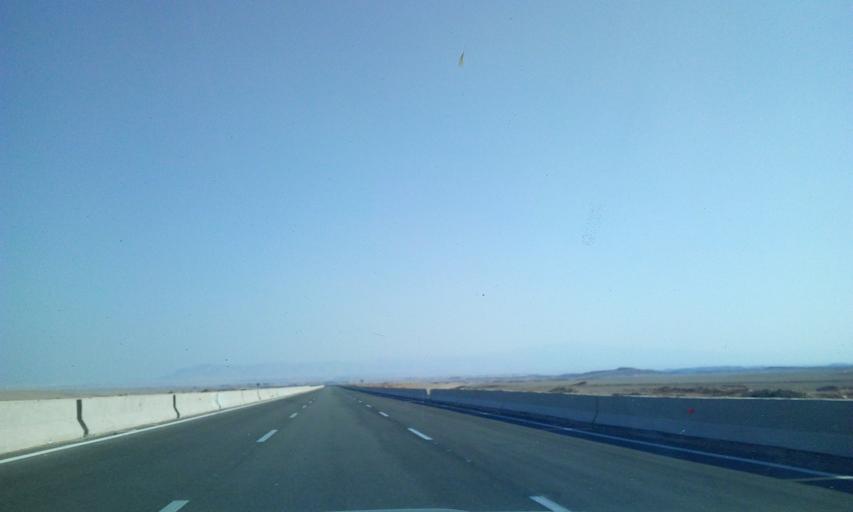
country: EG
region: As Suways
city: Ain Sukhna
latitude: 29.2093
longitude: 32.4933
